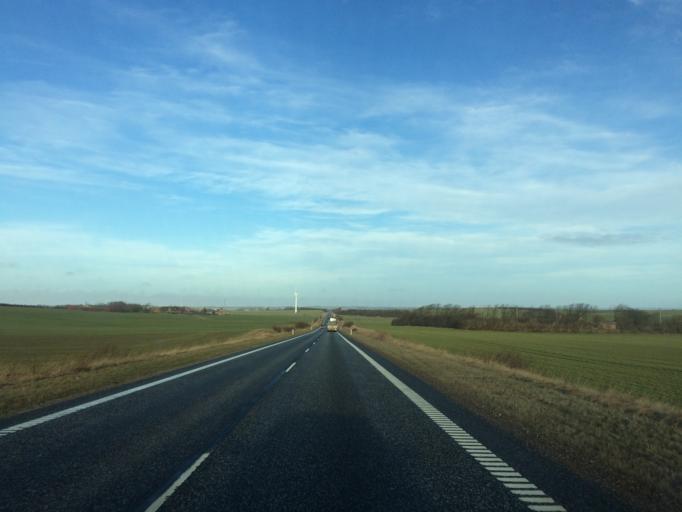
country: DK
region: North Denmark
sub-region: Thisted Kommune
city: Hurup
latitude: 56.7623
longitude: 8.4541
